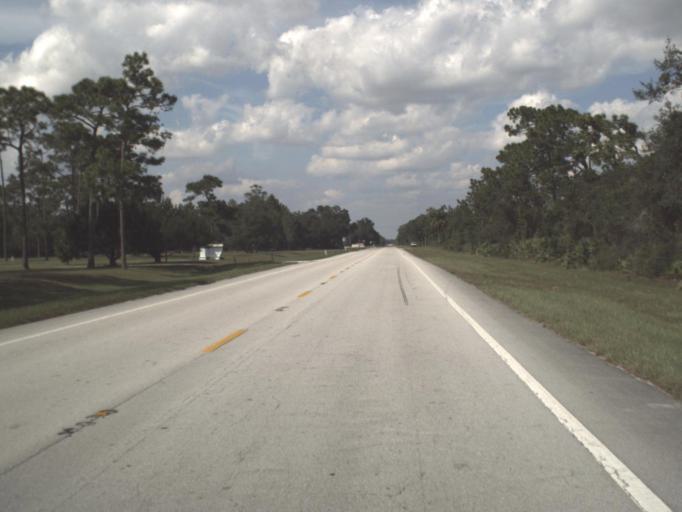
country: US
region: Florida
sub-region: Okeechobee County
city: Cypress Quarters
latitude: 27.5418
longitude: -80.8132
